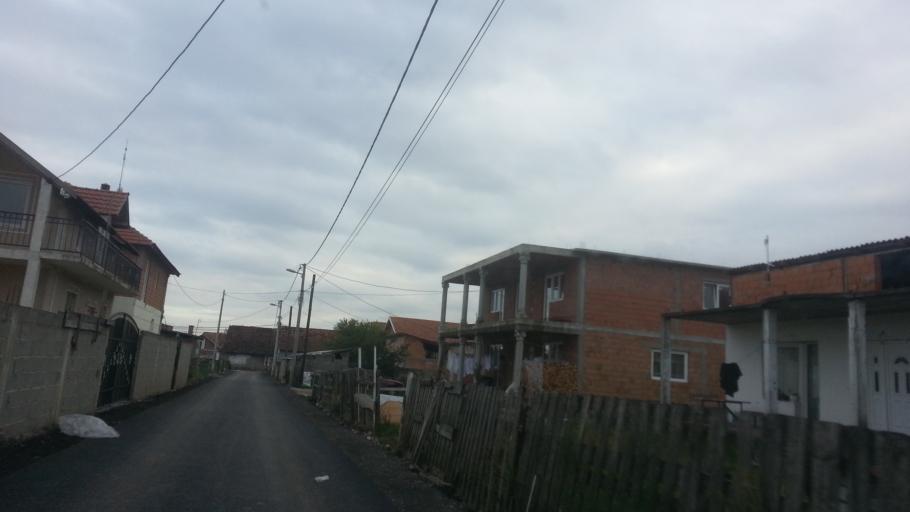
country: RS
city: Novi Banovci
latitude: 44.9177
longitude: 20.2727
